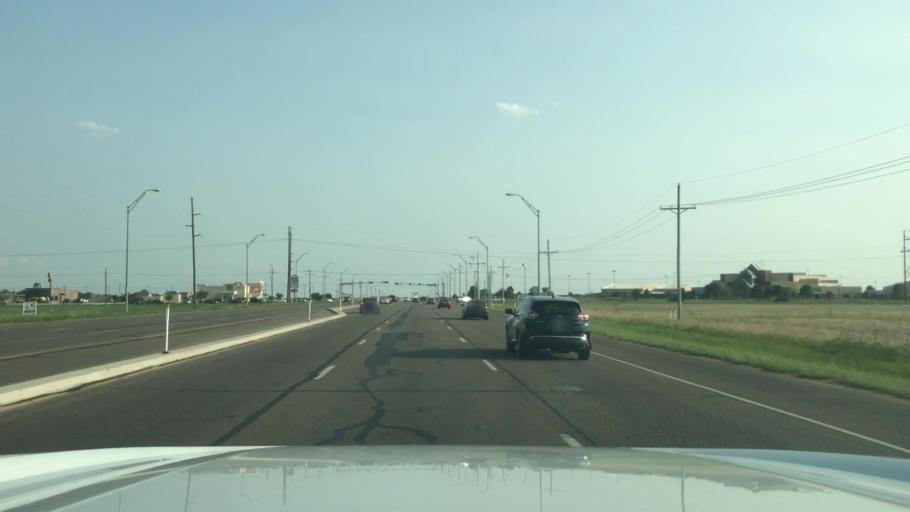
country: US
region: Texas
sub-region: Potter County
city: Amarillo
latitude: 35.1495
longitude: -101.9383
